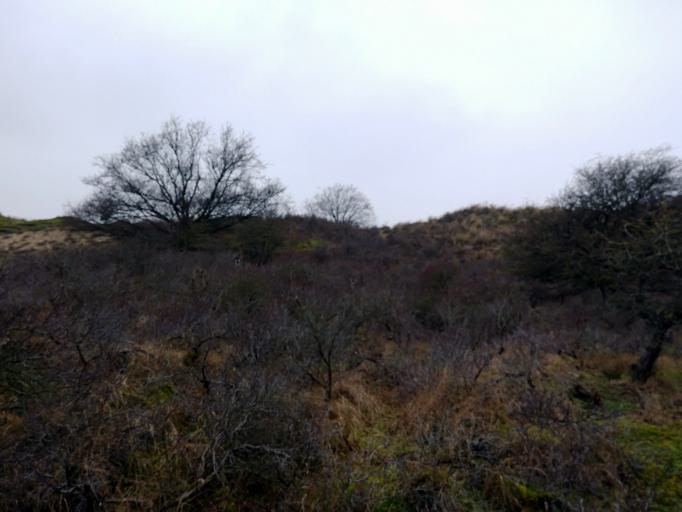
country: NL
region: North Holland
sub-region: Gemeente Zandvoort
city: Zandvoort
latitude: 52.3215
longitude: 4.5371
